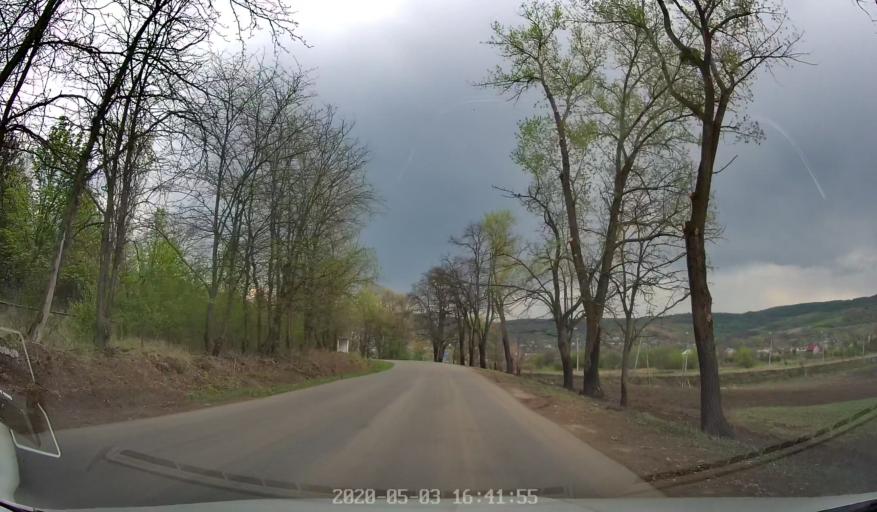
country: MD
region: Stinga Nistrului
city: Bucovat
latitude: 47.1626
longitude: 28.4143
